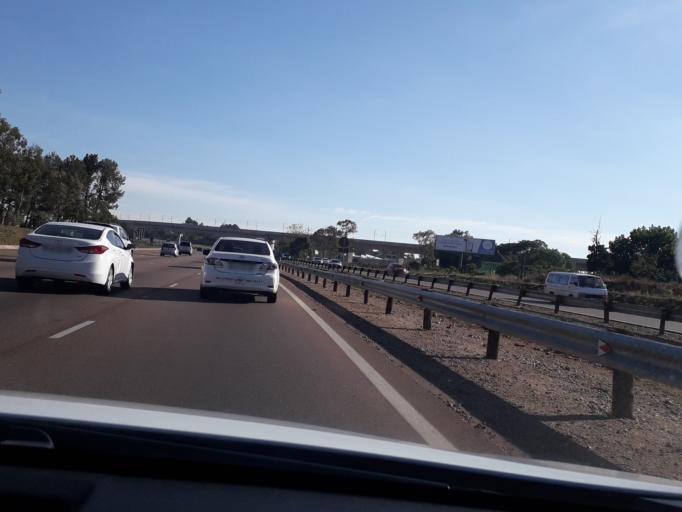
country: ZA
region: Gauteng
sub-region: City of Tshwane Metropolitan Municipality
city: Centurion
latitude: -25.8445
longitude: 28.1819
